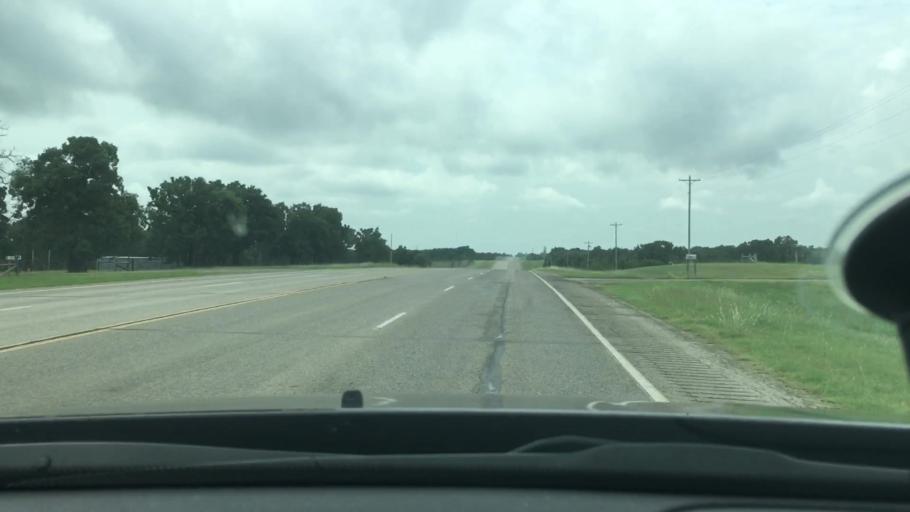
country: US
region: Oklahoma
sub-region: Carter County
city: Healdton
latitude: 34.1933
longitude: -97.4748
